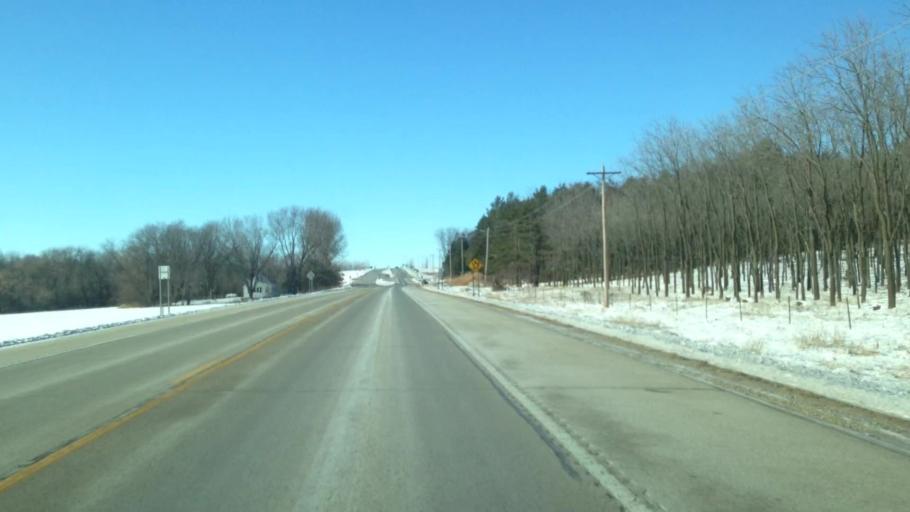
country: US
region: Minnesota
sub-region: Olmsted County
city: Oronoco
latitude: 44.1082
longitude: -92.5016
